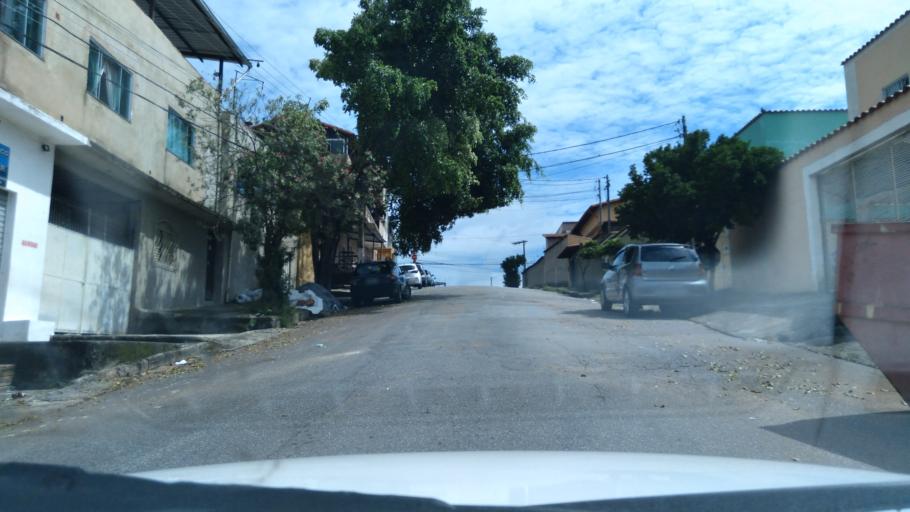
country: BR
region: Minas Gerais
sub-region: Belo Horizonte
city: Belo Horizonte
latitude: -19.9022
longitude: -43.8893
